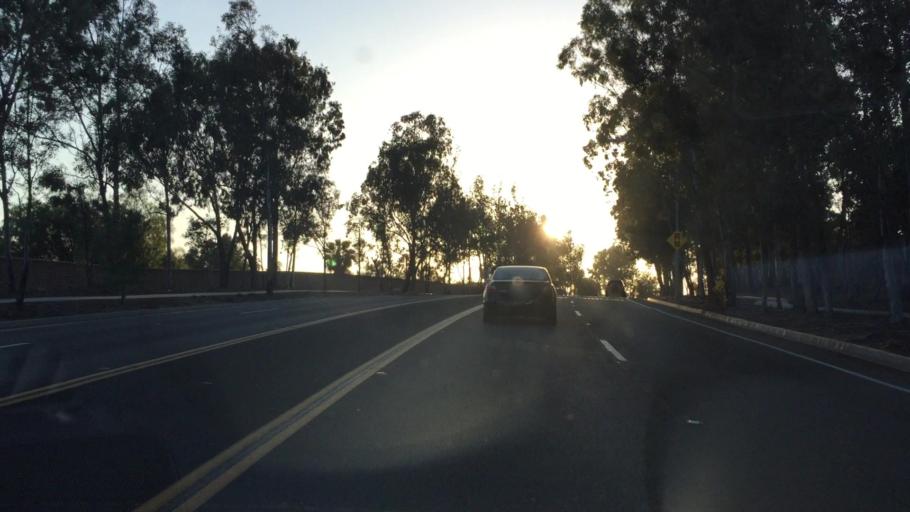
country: US
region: California
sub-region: San Diego County
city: Poway
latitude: 32.9787
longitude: -117.0561
